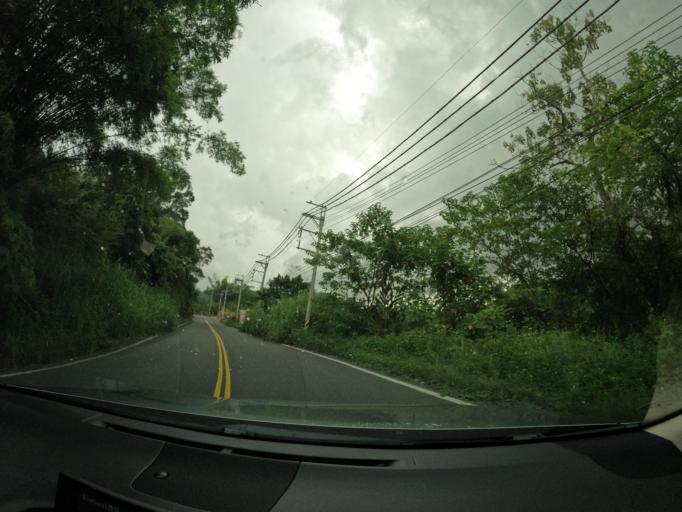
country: TW
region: Taiwan
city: Lugu
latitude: 23.8386
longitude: 120.7740
